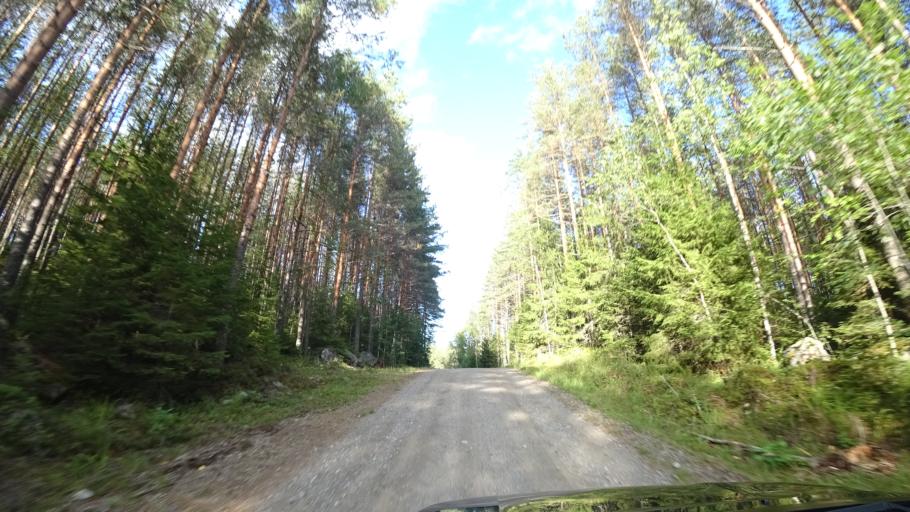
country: FI
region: Paijanne Tavastia
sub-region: Lahti
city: Auttoinen
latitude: 61.2217
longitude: 25.1845
